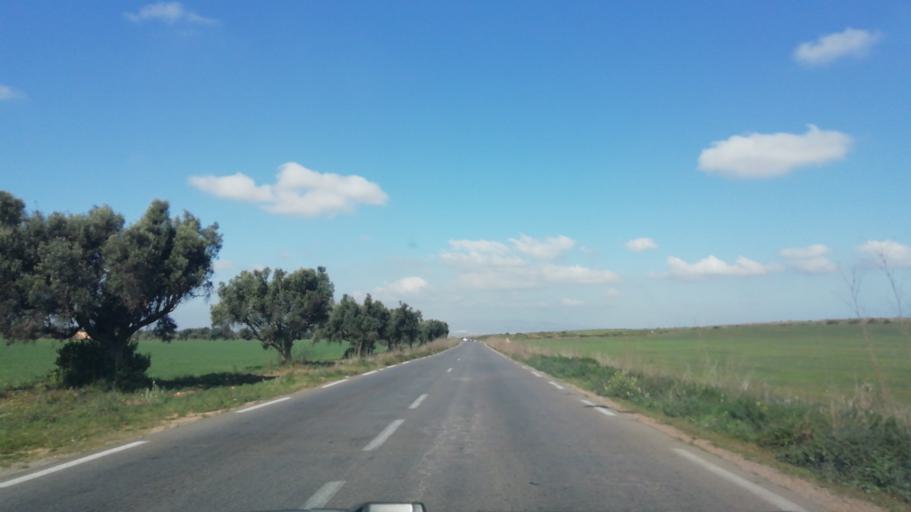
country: DZ
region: Oran
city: Ain el Bya
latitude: 35.7174
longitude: -0.2353
